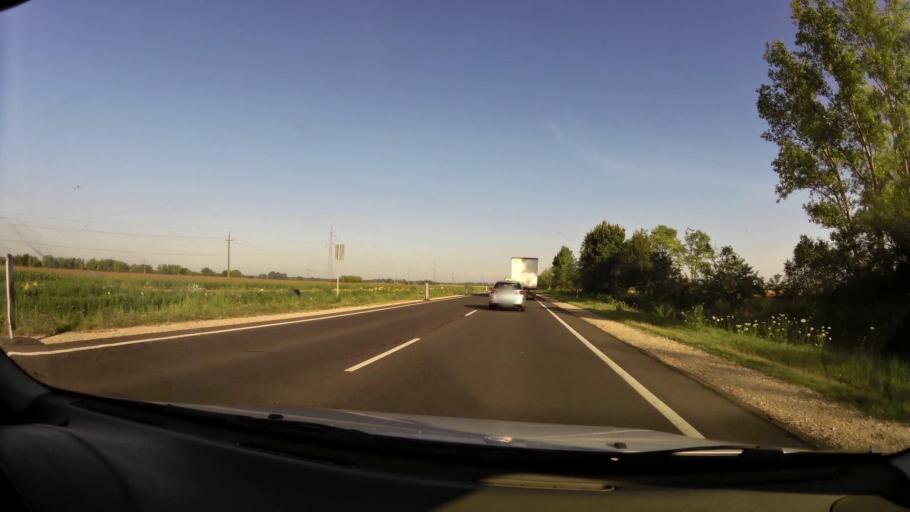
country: HU
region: Pest
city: Cegled
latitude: 47.2074
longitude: 19.7627
